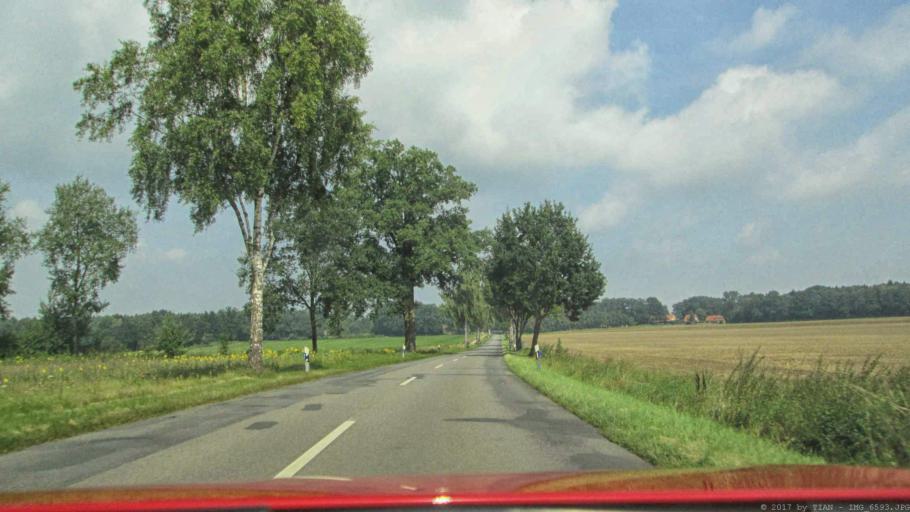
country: DE
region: Lower Saxony
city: Wrestedt
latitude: 52.9323
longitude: 10.5725
